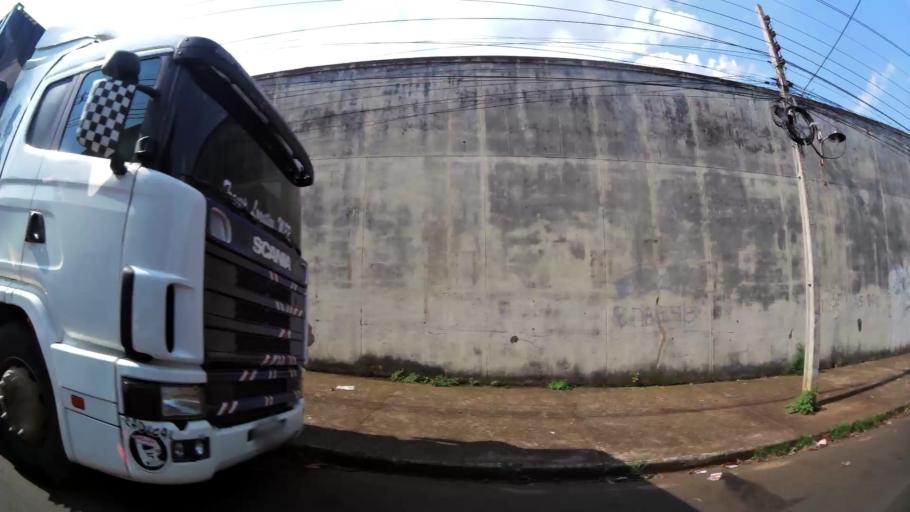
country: PY
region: Alto Parana
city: Ciudad del Este
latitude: -25.5034
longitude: -54.6312
